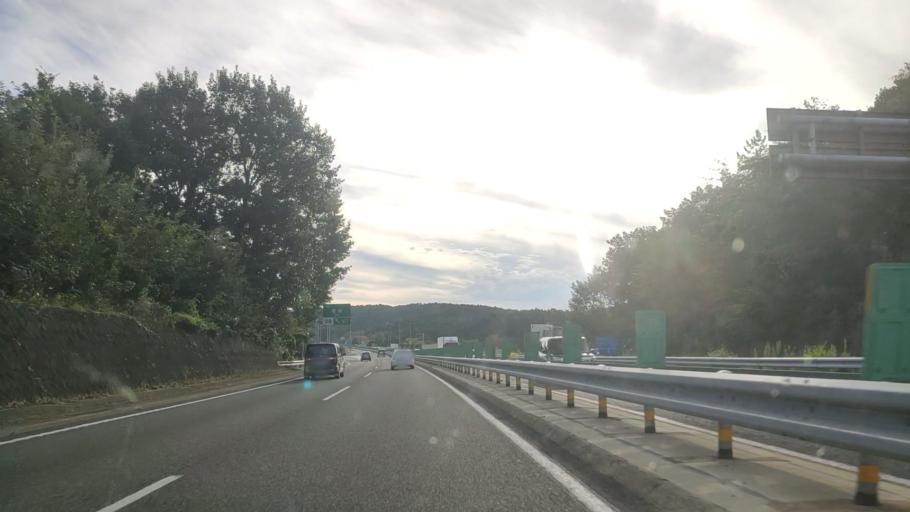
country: JP
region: Gifu
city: Nakatsugawa
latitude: 35.4555
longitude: 137.3986
